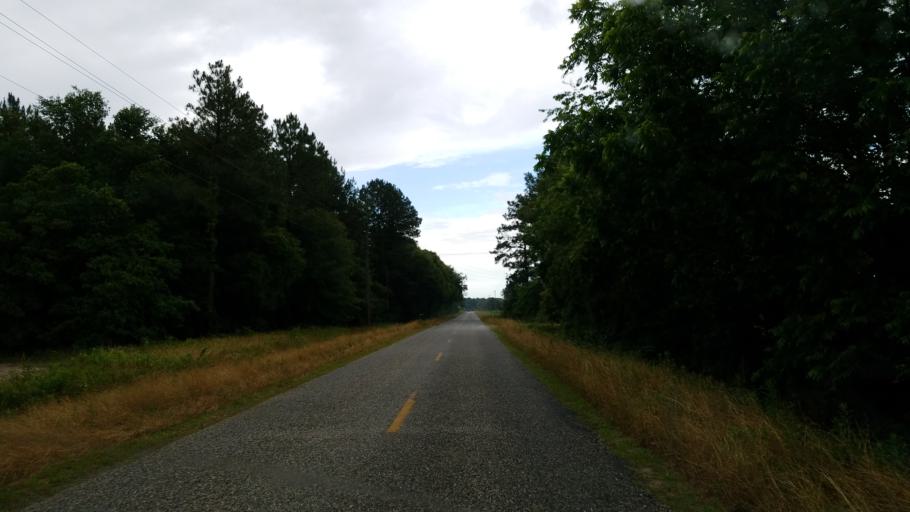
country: US
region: Georgia
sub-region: Crisp County
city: Cordele
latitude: 31.8351
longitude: -83.7799
